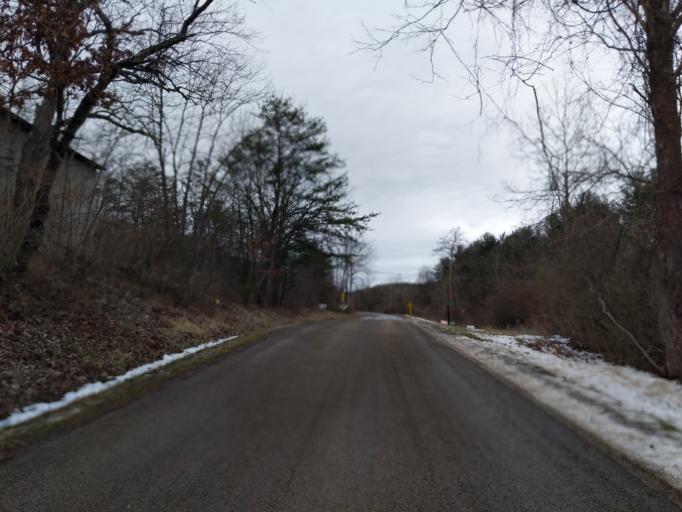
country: US
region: Ohio
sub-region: Athens County
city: The Plains
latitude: 39.3326
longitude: -82.1380
